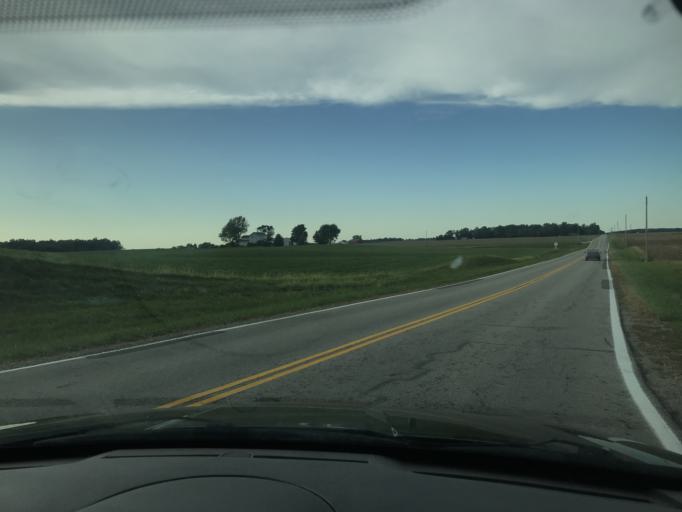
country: US
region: Ohio
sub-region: Logan County
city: West Liberty
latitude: 40.2111
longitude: -83.7016
